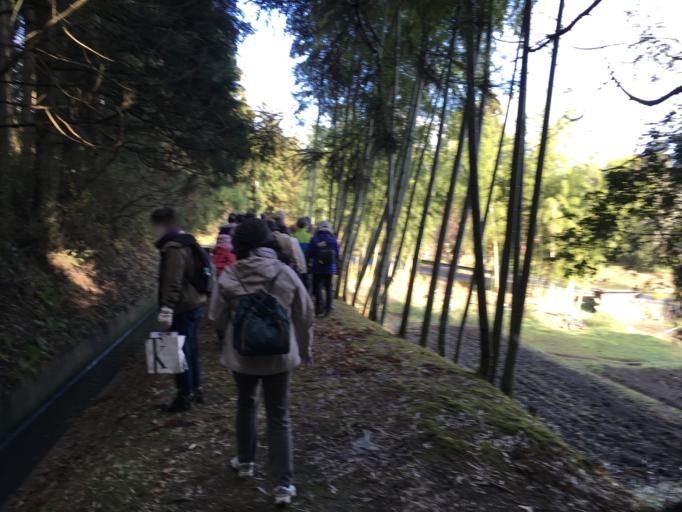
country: JP
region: Iwate
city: Ichinoseki
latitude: 38.9817
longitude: 141.1031
